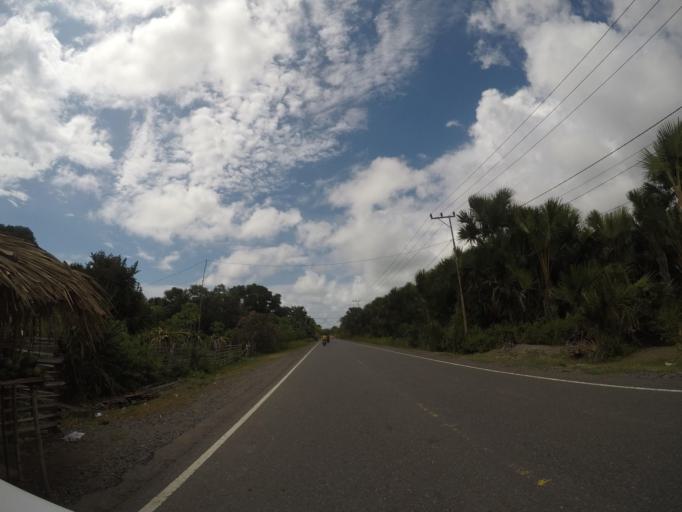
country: TL
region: Liquica
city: Maubara
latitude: -8.7252
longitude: 125.1129
